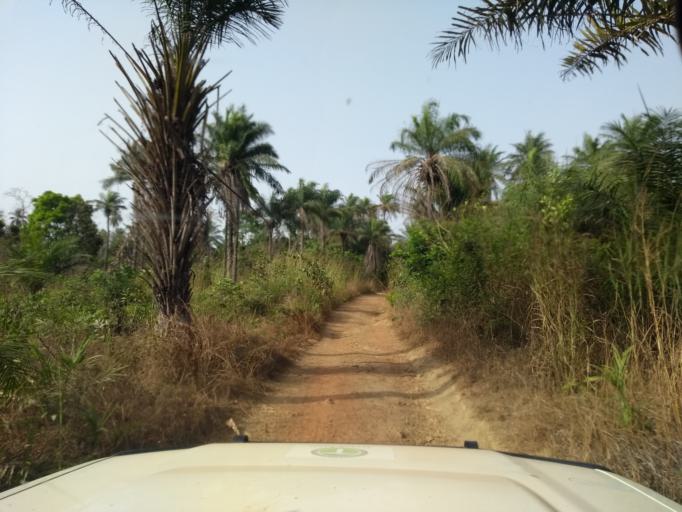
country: GN
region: Kindia
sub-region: Prefecture de Dubreka
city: Dubreka
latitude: 9.8199
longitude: -13.5558
